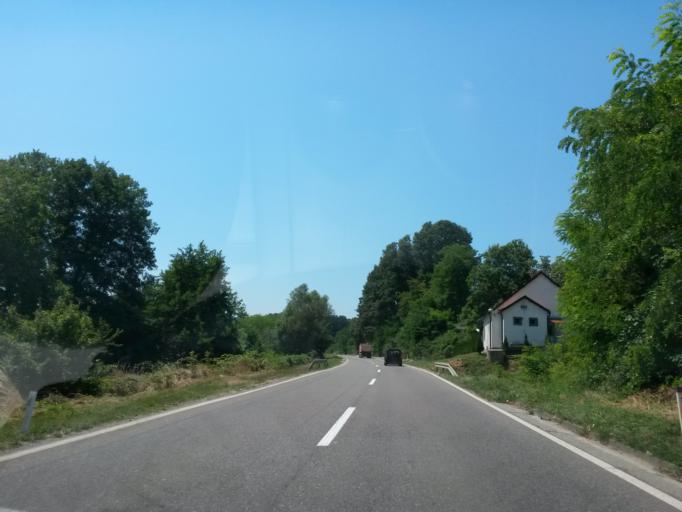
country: BA
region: Federation of Bosnia and Herzegovina
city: Odzak
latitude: 44.9573
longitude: 18.2168
